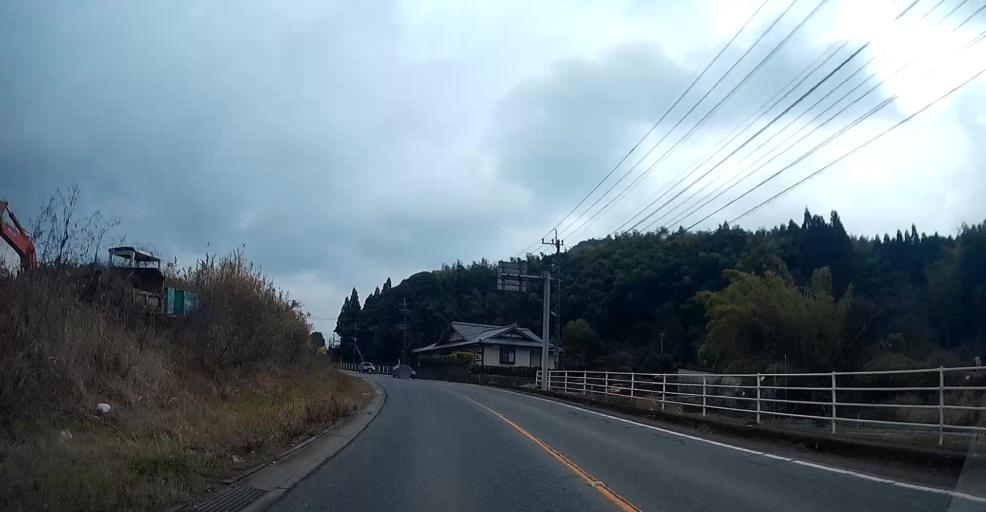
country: JP
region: Kumamoto
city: Matsubase
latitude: 32.6459
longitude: 130.7288
